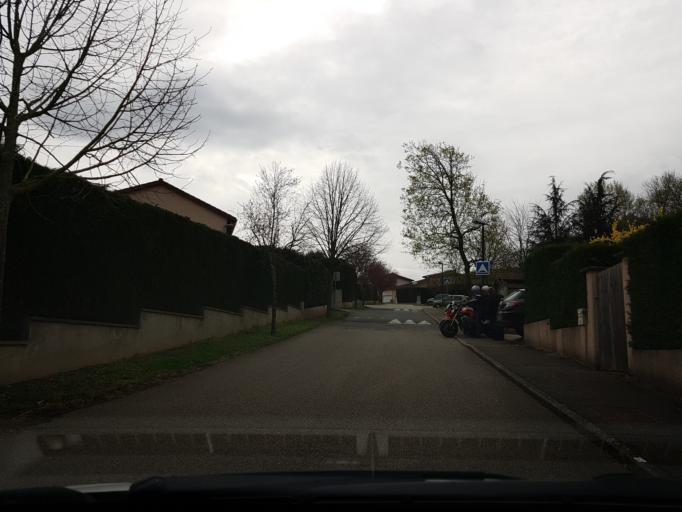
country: FR
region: Rhone-Alpes
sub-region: Departement de l'Ain
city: Trevoux
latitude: 45.9486
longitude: 4.7626
